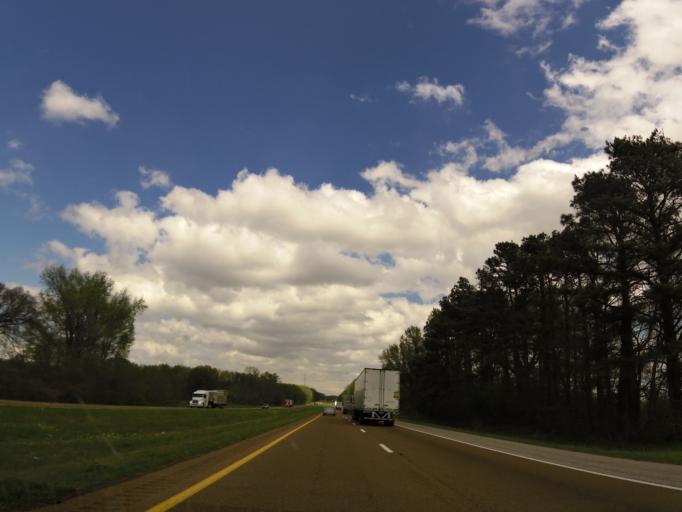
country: US
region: Tennessee
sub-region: Tipton County
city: Mason
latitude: 35.3649
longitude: -89.4834
